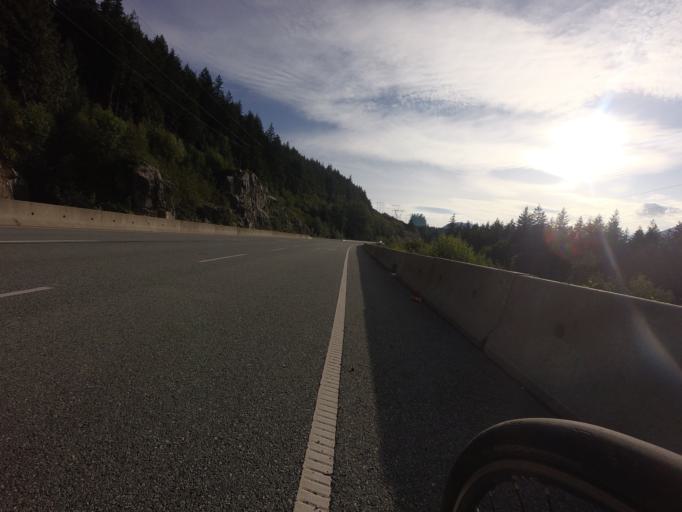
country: CA
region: British Columbia
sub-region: Greater Vancouver Regional District
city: Lions Bay
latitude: 49.6549
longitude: -123.1896
